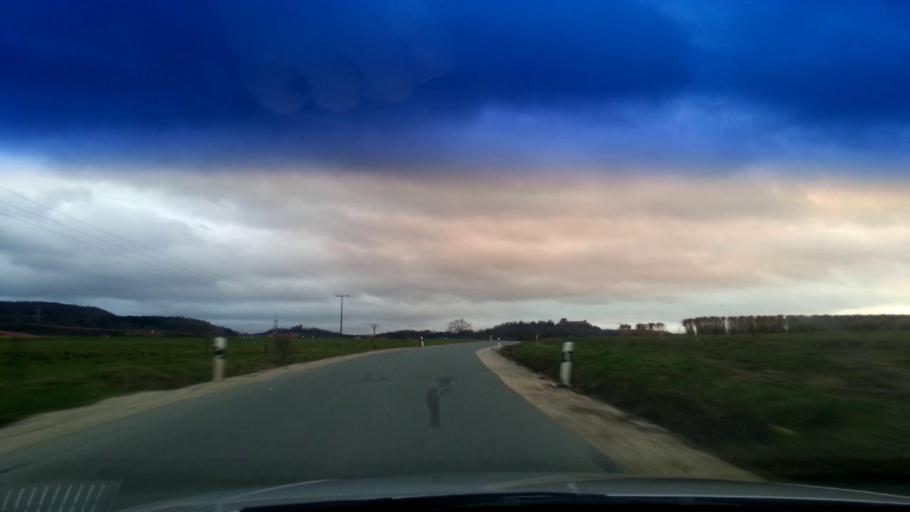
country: DE
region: Bavaria
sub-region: Upper Franconia
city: Schesslitz
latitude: 49.9754
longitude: 11.0586
